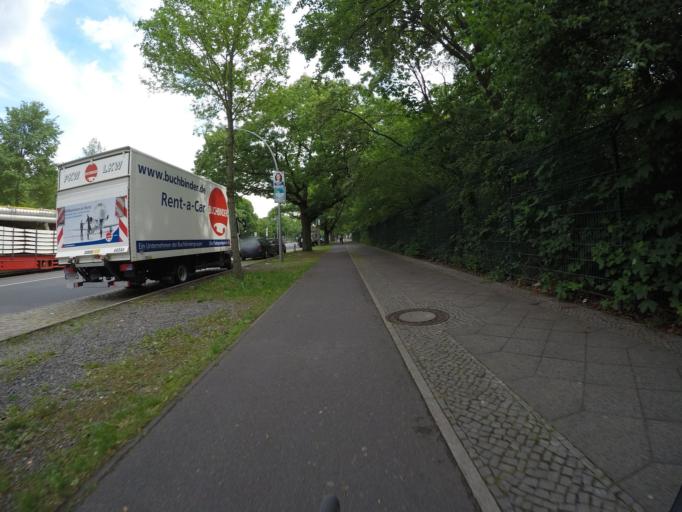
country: DE
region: Berlin
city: Tempelhof Bezirk
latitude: 52.4808
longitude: 13.4140
